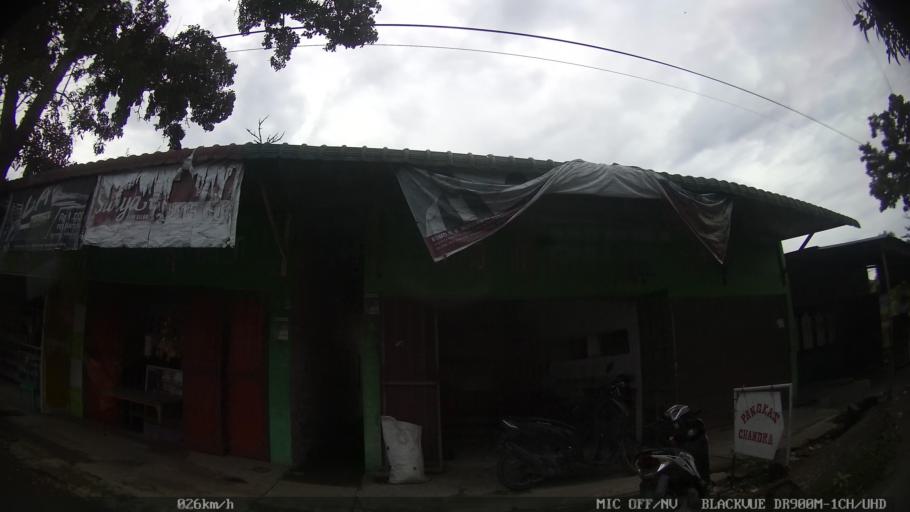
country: ID
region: North Sumatra
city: Sunggal
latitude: 3.5941
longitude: 98.5659
